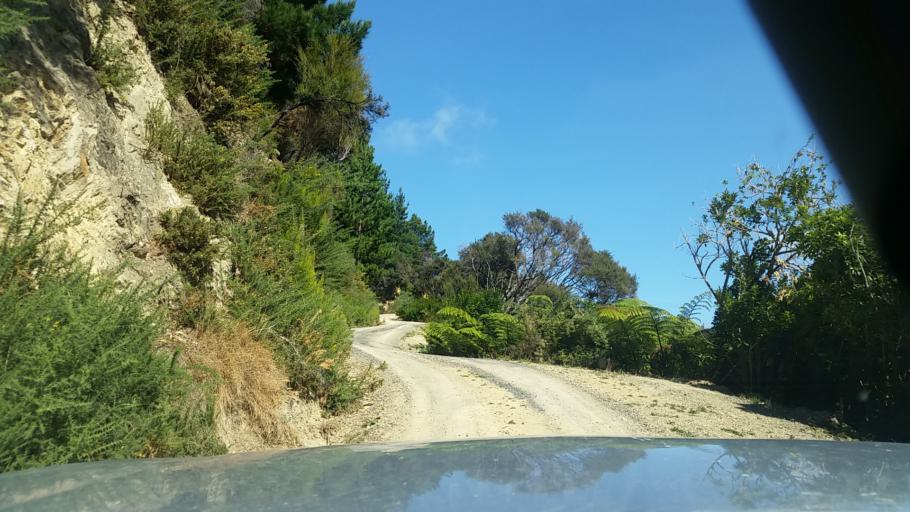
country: NZ
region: Marlborough
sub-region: Marlborough District
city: Picton
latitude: -41.3077
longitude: 174.1732
